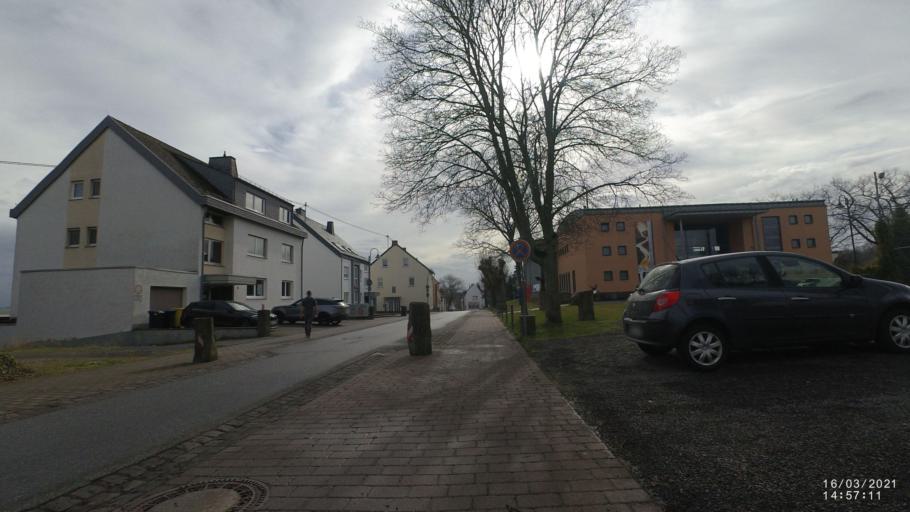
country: DE
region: Rheinland-Pfalz
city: Mendig
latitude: 50.3762
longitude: 7.2834
